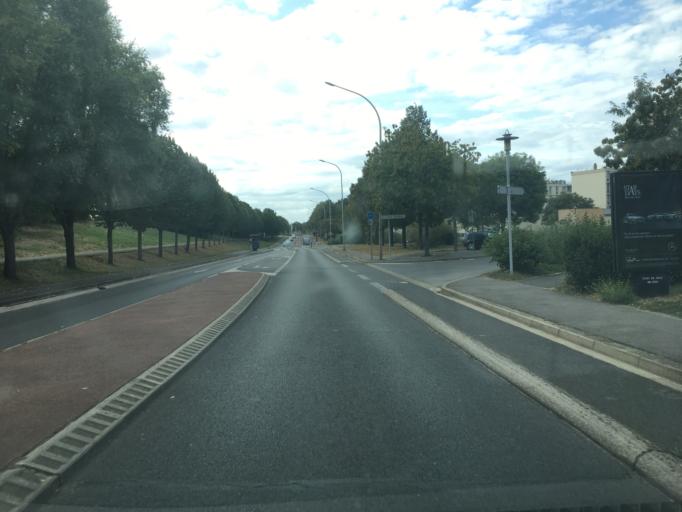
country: FR
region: Ile-de-France
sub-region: Departement du Val-de-Marne
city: Valenton
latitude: 48.7477
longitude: 2.4611
